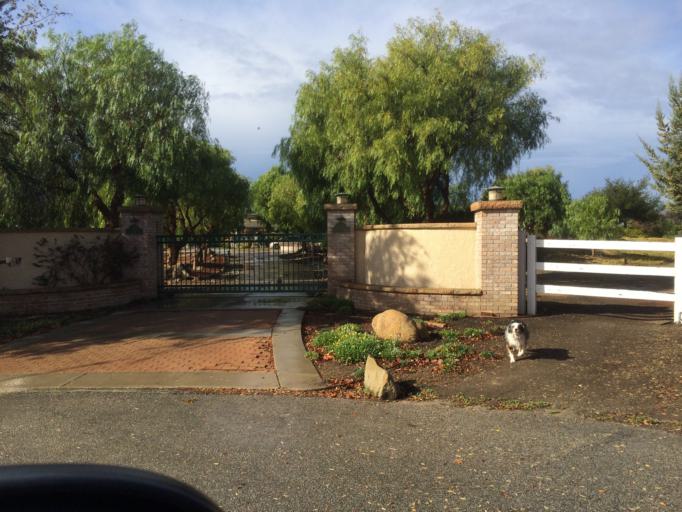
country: US
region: California
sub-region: San Luis Obispo County
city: Pismo Beach
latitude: 35.2110
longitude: -120.6042
